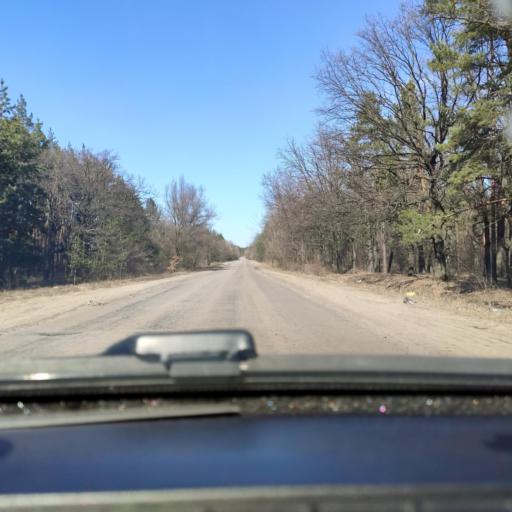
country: RU
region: Voronezj
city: Somovo
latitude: 51.7146
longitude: 39.3668
